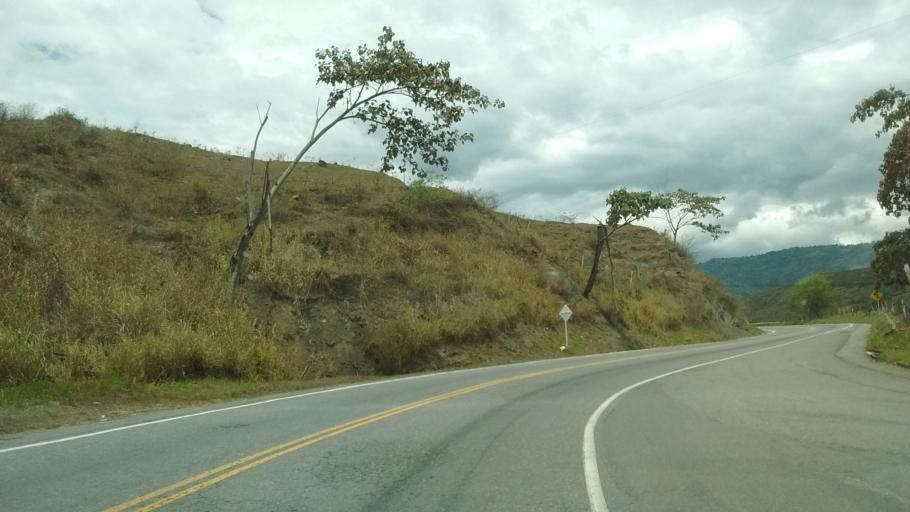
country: CO
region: Cauca
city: La Sierra
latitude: 2.2068
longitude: -76.8035
